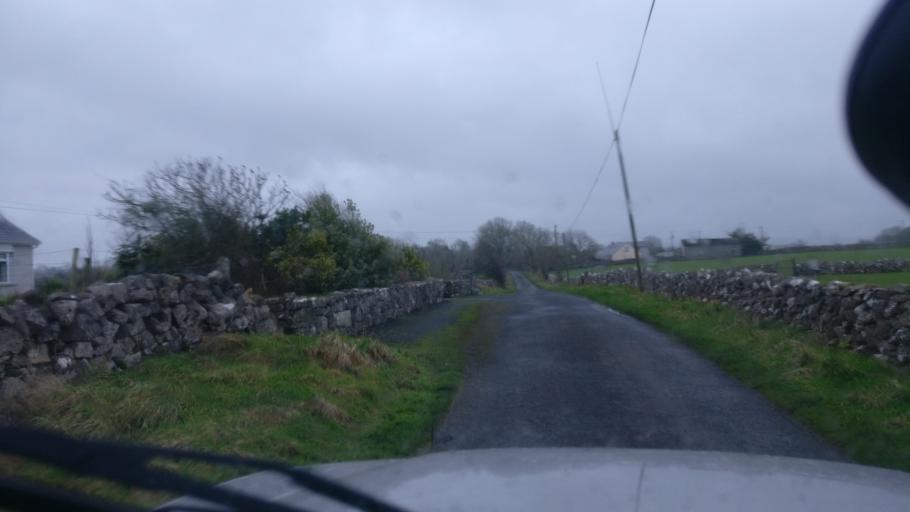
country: IE
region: Connaught
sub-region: County Galway
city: Loughrea
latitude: 53.2192
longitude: -8.5902
